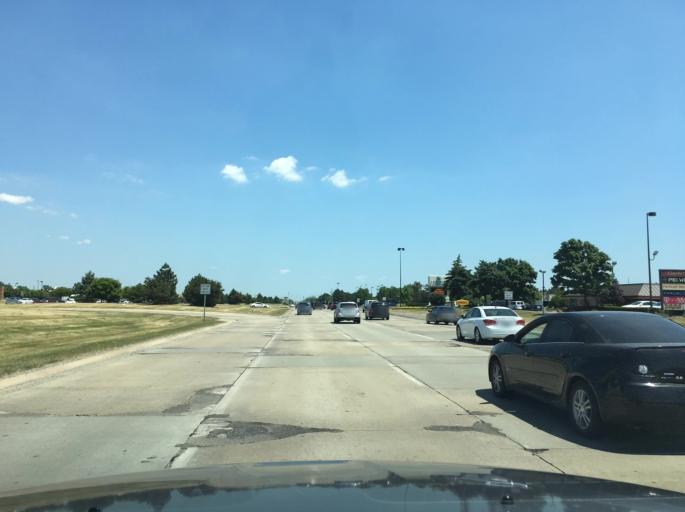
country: US
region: Michigan
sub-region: Macomb County
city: Utica
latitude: 42.6269
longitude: -82.9881
